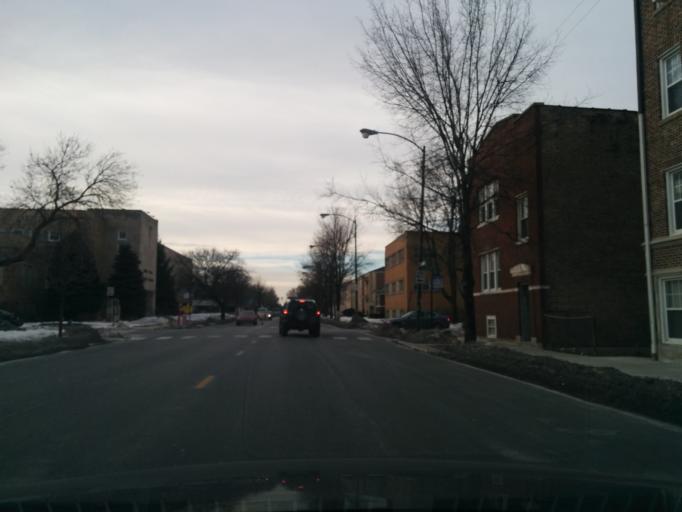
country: US
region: Illinois
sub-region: Cook County
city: Harwood Heights
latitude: 41.9518
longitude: -87.7670
